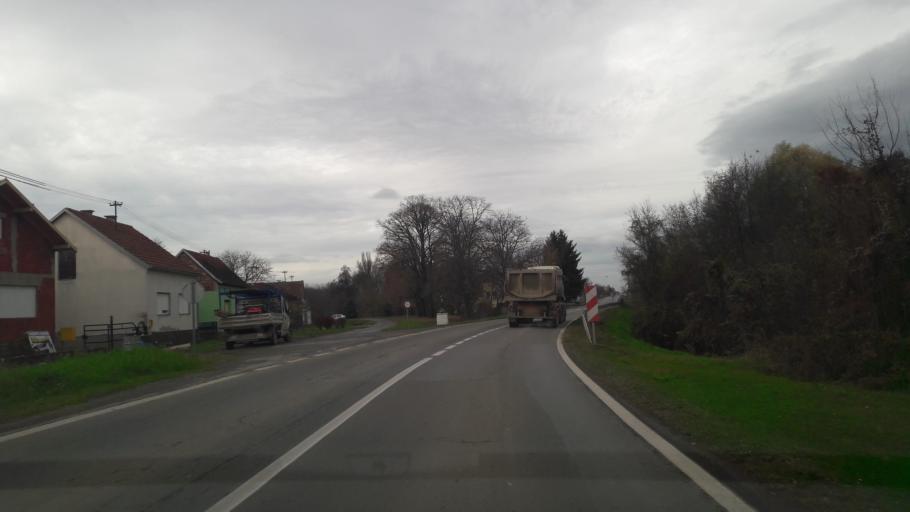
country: HR
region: Osjecko-Baranjska
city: Fericanci
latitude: 45.5244
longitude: 17.9672
